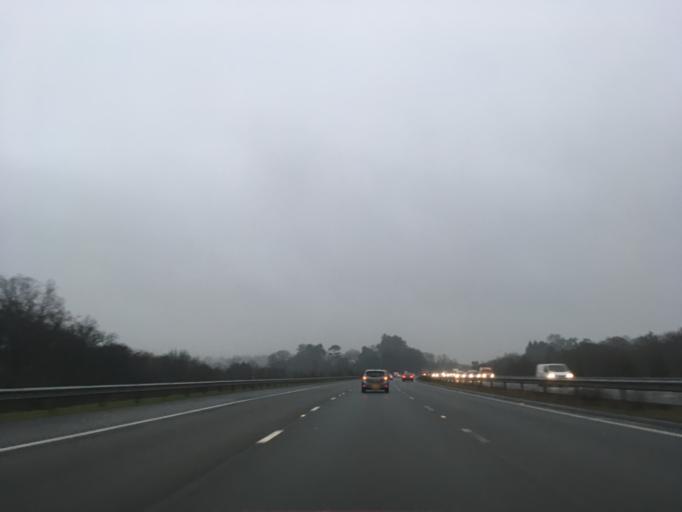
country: GB
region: Wales
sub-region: Caerphilly County Borough
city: Caerphilly
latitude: 51.5388
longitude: -3.2133
